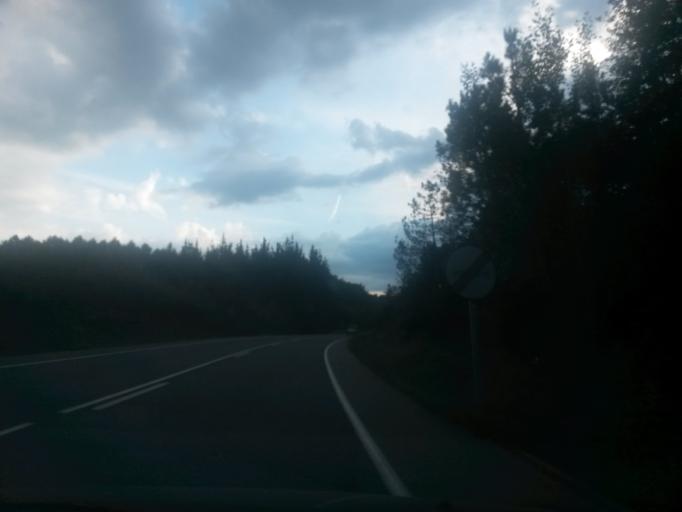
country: ES
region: Catalonia
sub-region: Provincia de Girona
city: Brunyola
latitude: 41.9042
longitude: 2.6626
